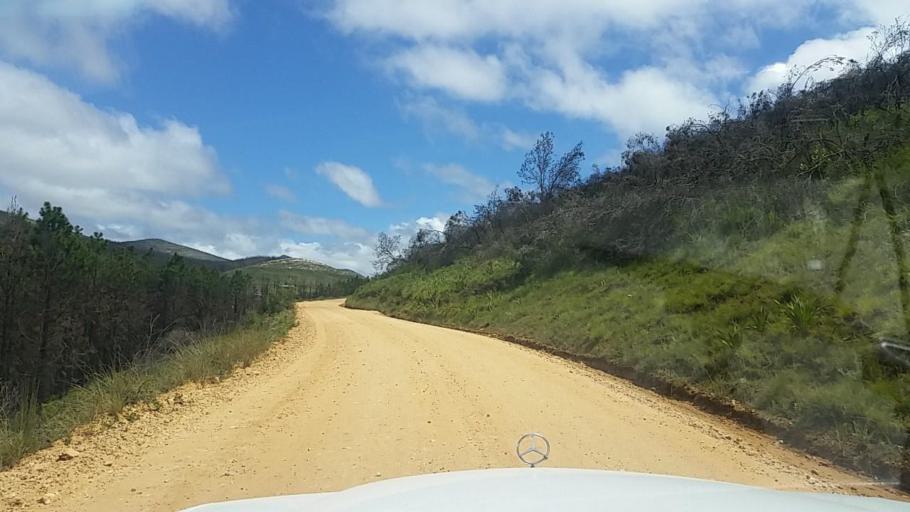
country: ZA
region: Western Cape
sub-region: Eden District Municipality
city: Knysna
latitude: -33.8911
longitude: 23.1708
